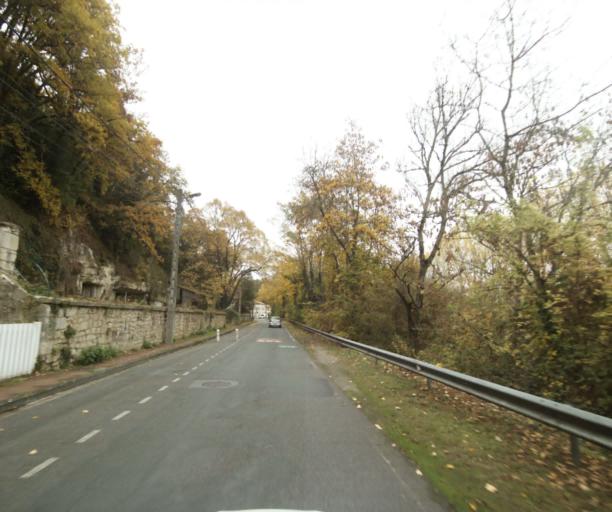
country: FR
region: Poitou-Charentes
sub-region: Departement de la Charente-Maritime
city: Saintes
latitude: 45.7334
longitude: -0.6397
